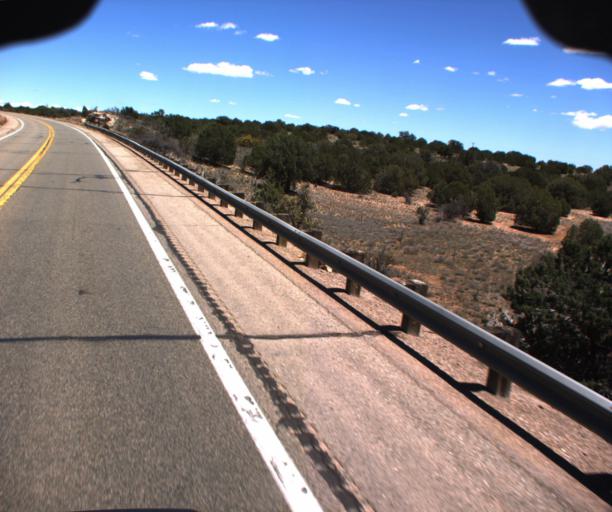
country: US
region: Arizona
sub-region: Yavapai County
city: Paulden
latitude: 34.9319
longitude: -112.4391
